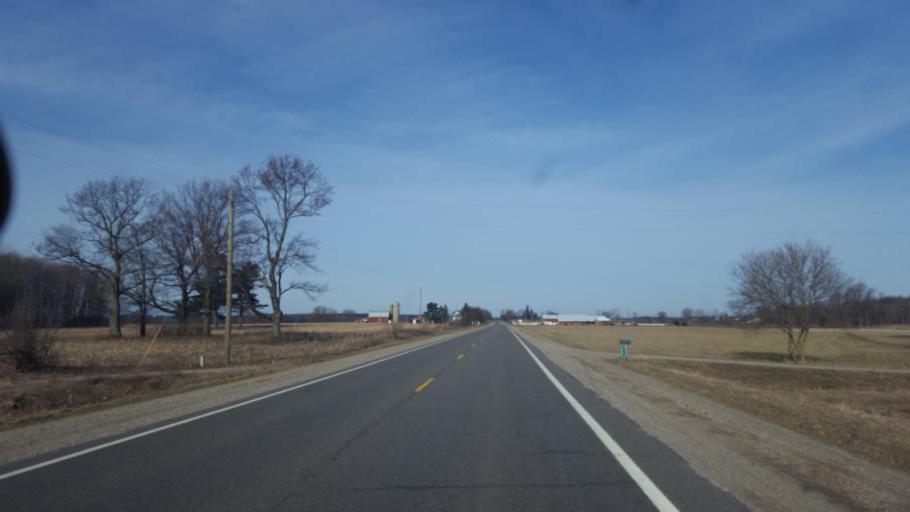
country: US
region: Michigan
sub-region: Montcalm County
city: Lakeview
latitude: 43.4314
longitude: -85.2976
